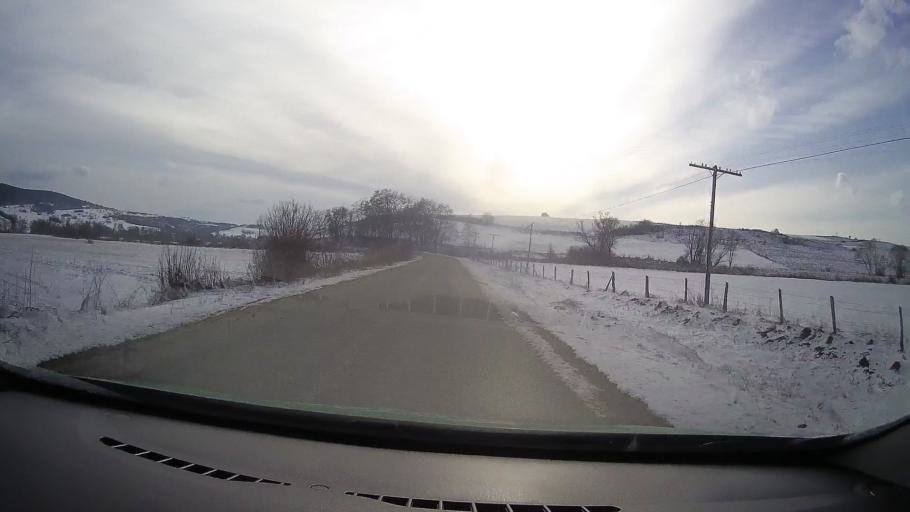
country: RO
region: Sibiu
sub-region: Comuna Iacobeni
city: Iacobeni
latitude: 46.0263
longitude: 24.7078
